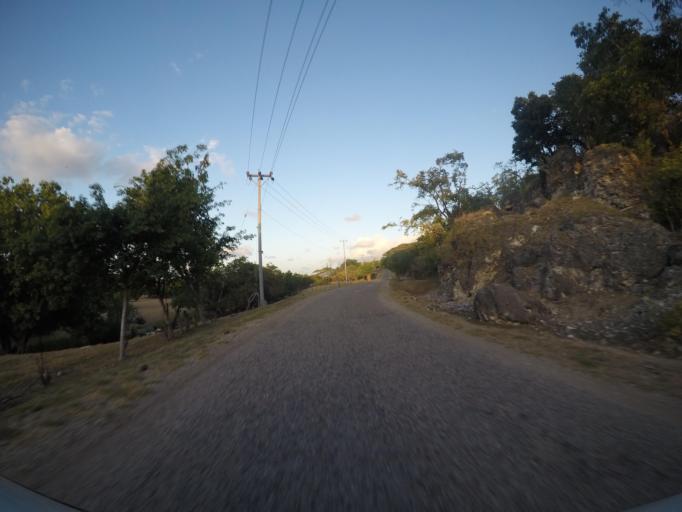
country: TL
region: Lautem
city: Lospalos
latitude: -8.3432
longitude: 127.0402
